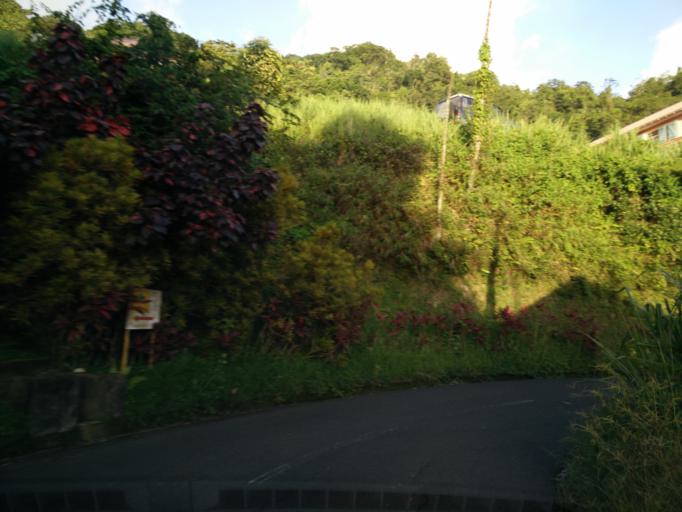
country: MQ
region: Martinique
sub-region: Martinique
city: Le Morne-Rouge
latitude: 14.7367
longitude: -61.1319
